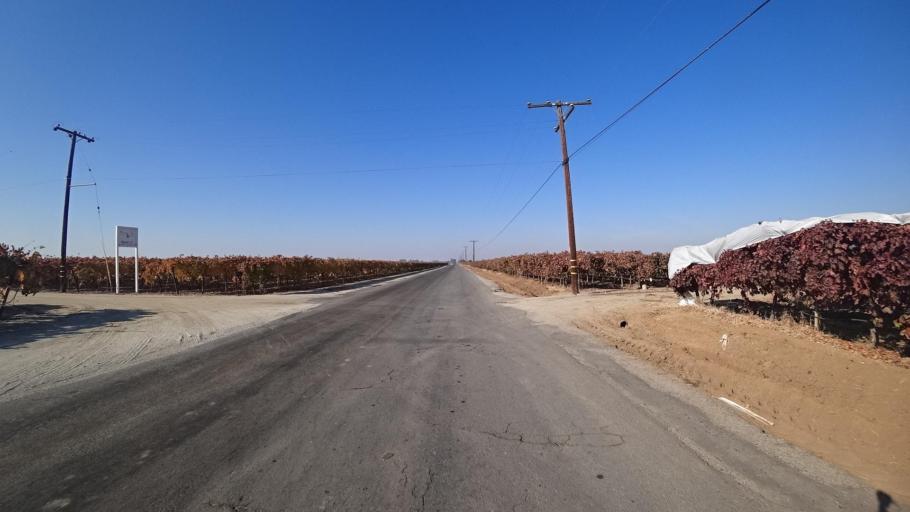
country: US
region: California
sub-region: Tulare County
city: Richgrove
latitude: 35.7471
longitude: -119.1472
